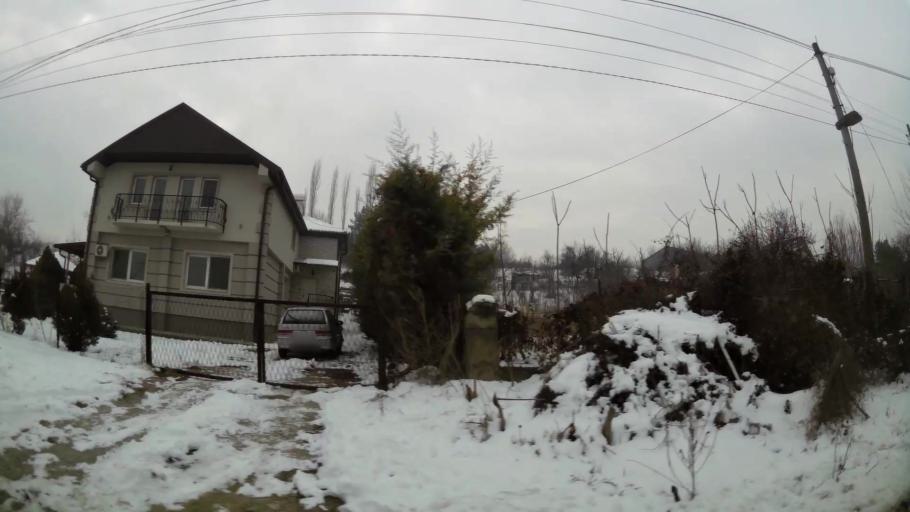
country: MK
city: Kondovo
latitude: 42.0472
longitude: 21.3450
